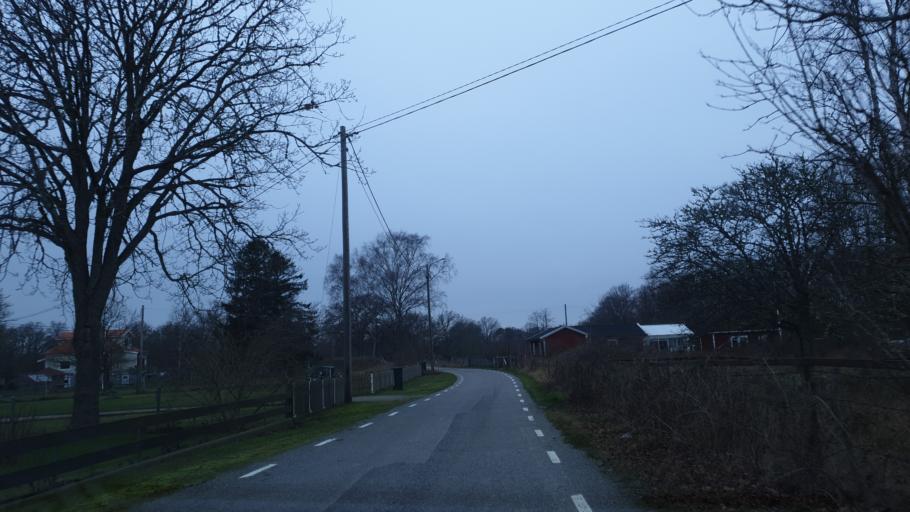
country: SE
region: Blekinge
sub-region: Karlskrona Kommun
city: Karlskrona
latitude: 56.1051
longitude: 15.6083
